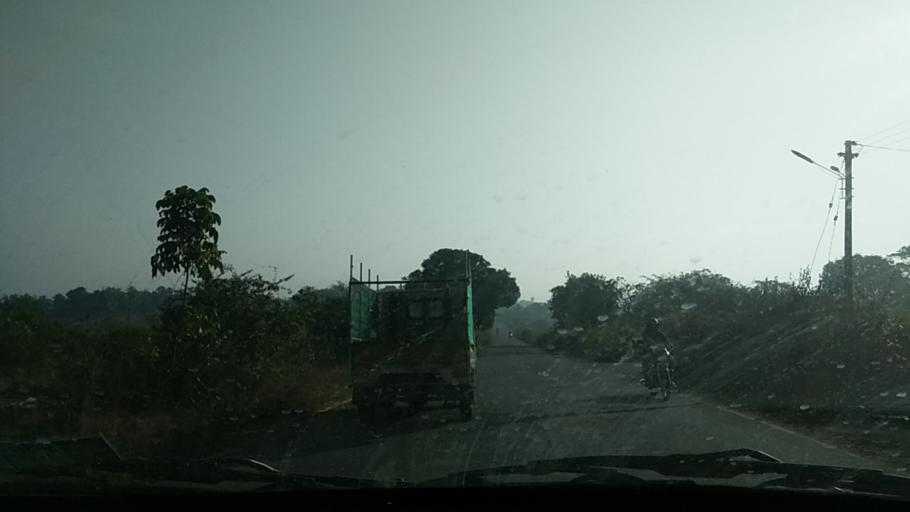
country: IN
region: Goa
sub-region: South Goa
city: Quepem
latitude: 15.1931
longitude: 74.0476
